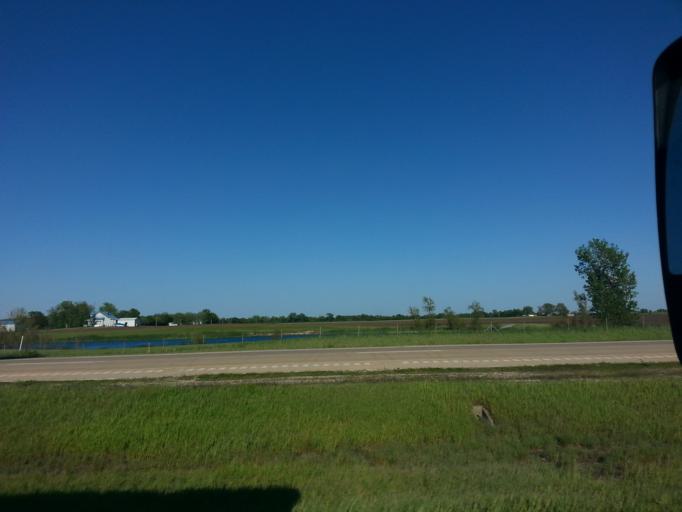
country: US
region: Illinois
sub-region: Woodford County
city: Minonk
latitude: 40.9756
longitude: -89.0565
